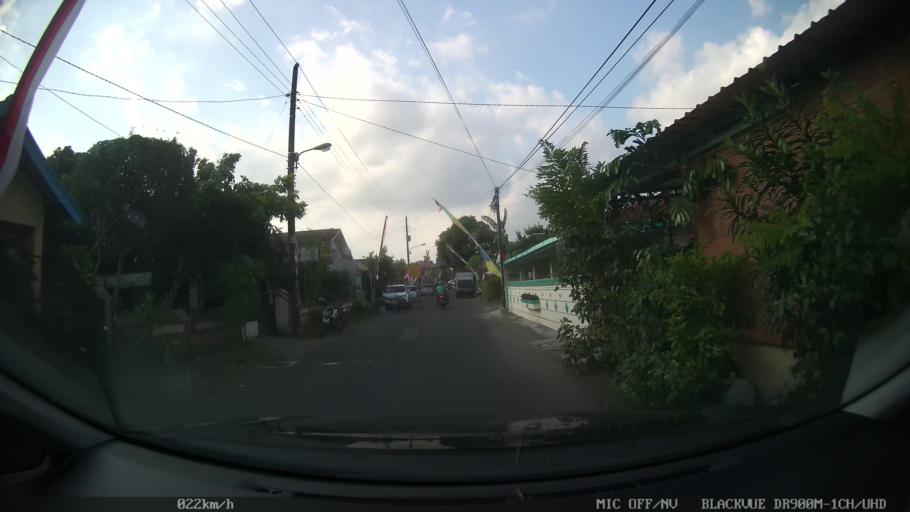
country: ID
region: Daerah Istimewa Yogyakarta
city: Yogyakarta
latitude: -7.7898
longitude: 110.3511
